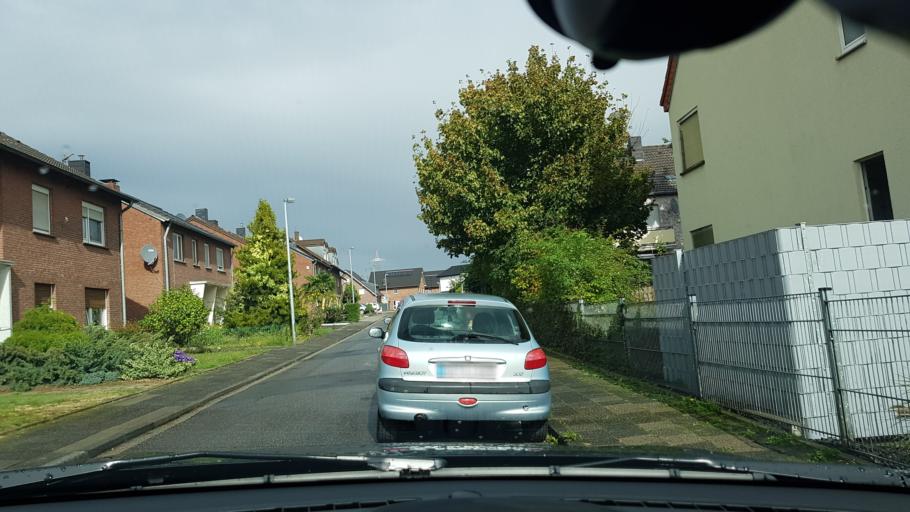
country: DE
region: North Rhine-Westphalia
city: Huckelhoven
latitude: 51.0589
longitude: 6.1989
